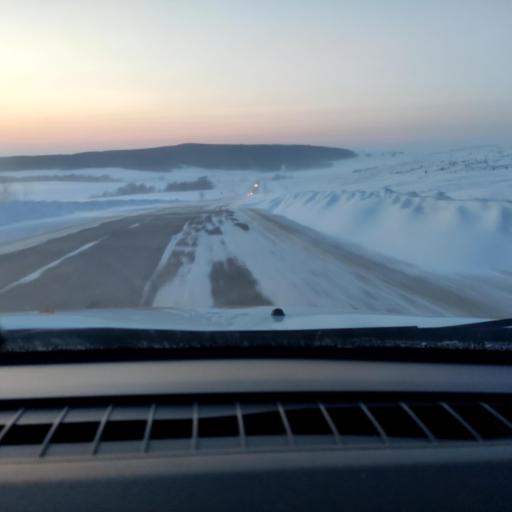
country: RU
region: Samara
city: Kinel'
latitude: 53.4376
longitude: 50.6673
